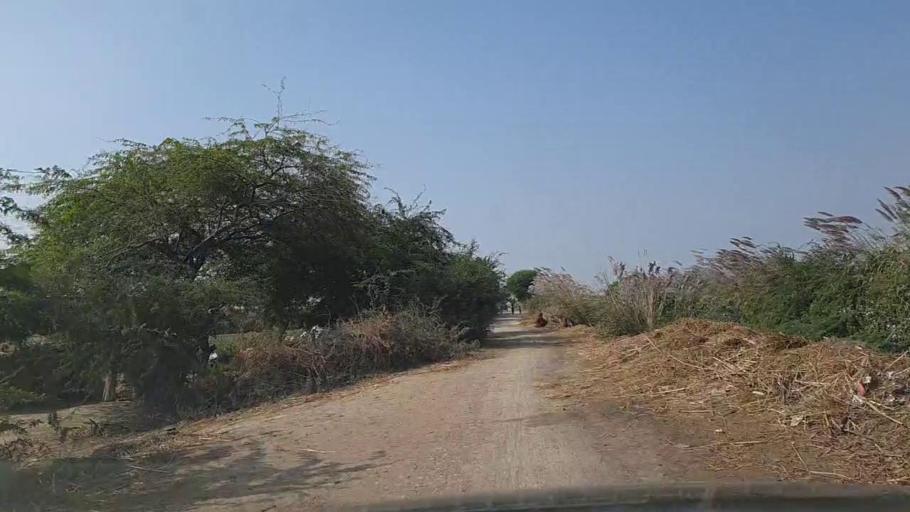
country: PK
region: Sindh
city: Gharo
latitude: 24.7032
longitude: 67.6425
